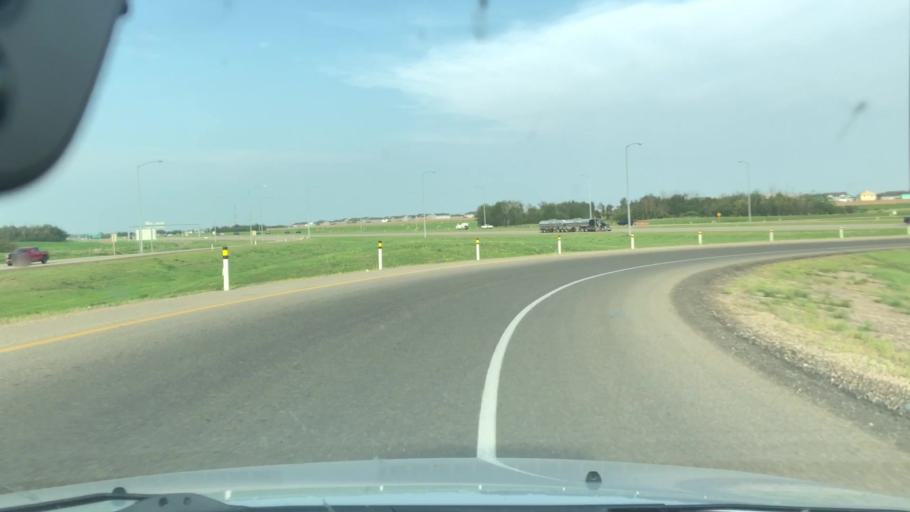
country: CA
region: Alberta
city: St. Albert
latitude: 53.6410
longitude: -113.5448
